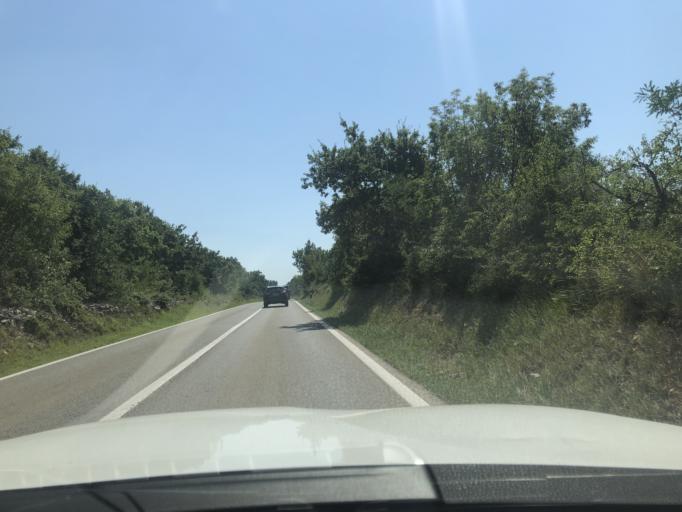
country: HR
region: Istarska
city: Vodnjan
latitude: 45.0212
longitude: 13.8024
